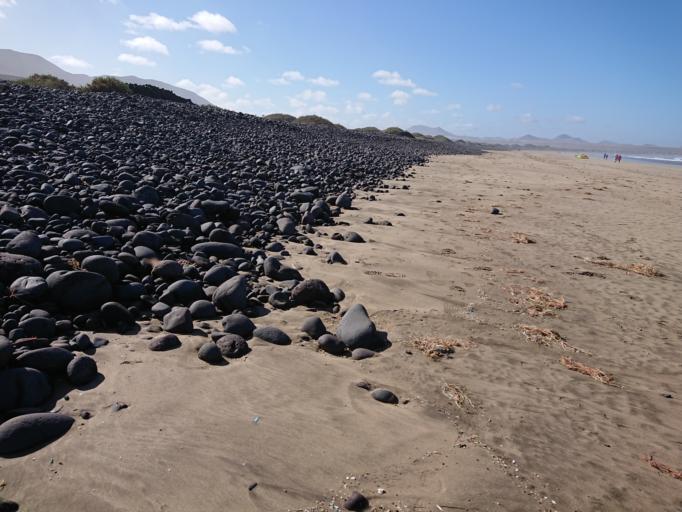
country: ES
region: Canary Islands
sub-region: Provincia de Las Palmas
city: Haria
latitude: 29.1207
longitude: -13.5438
